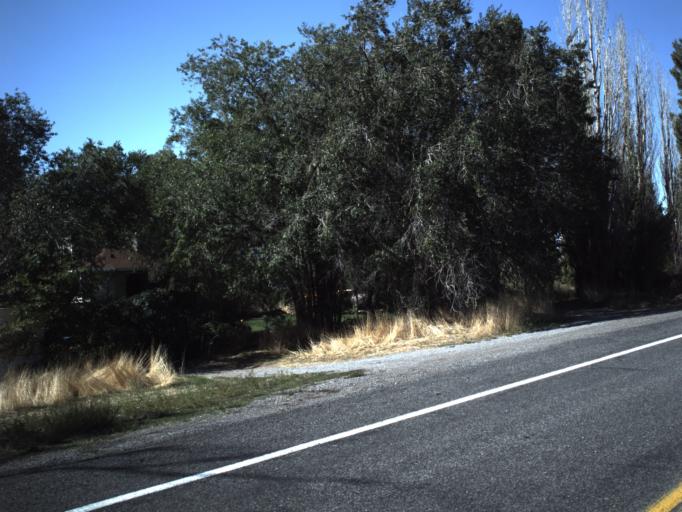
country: US
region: Utah
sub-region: Millard County
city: Fillmore
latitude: 39.1050
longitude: -112.2709
